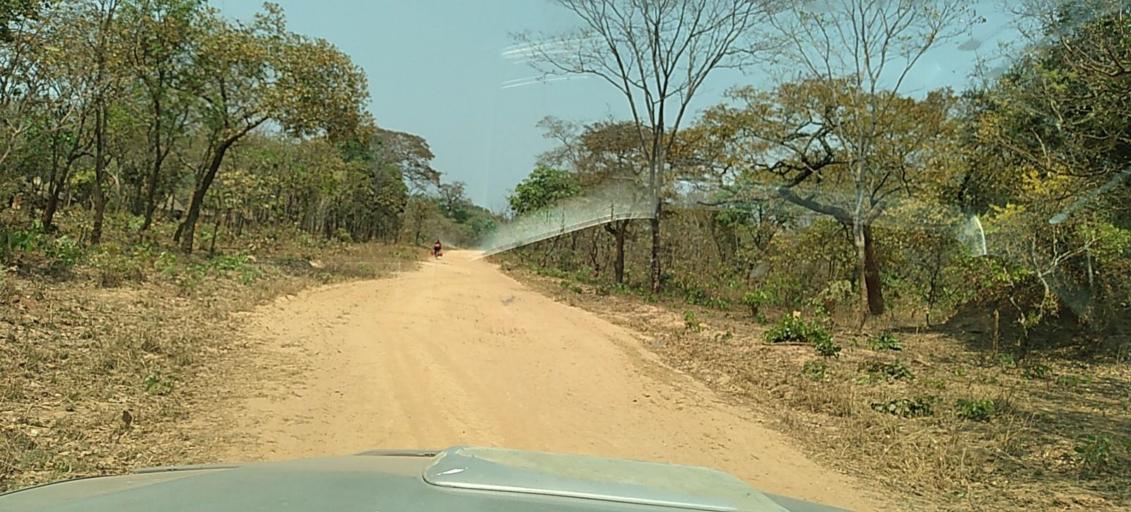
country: ZM
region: North-Western
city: Kasempa
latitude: -13.6548
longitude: 26.2578
